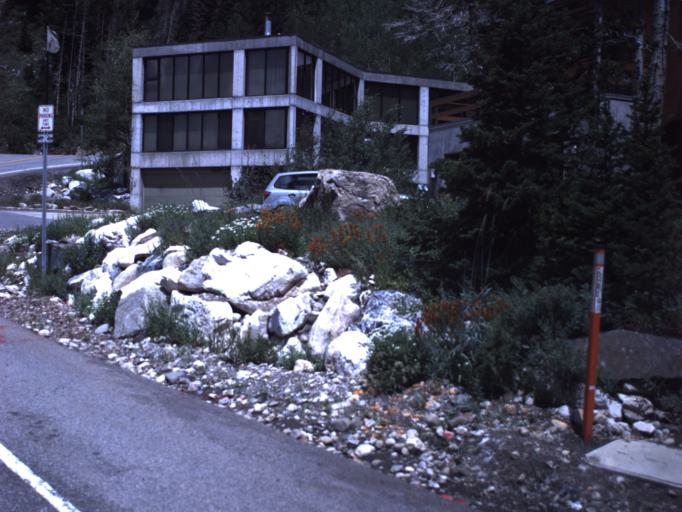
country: US
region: Utah
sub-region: Summit County
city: Snyderville
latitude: 40.5883
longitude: -111.6447
